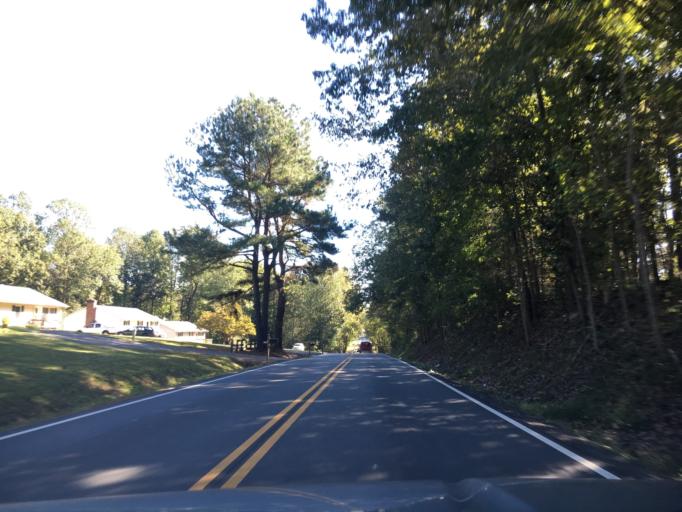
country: US
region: Virginia
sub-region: Goochland County
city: Goochland
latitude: 37.6970
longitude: -77.8798
